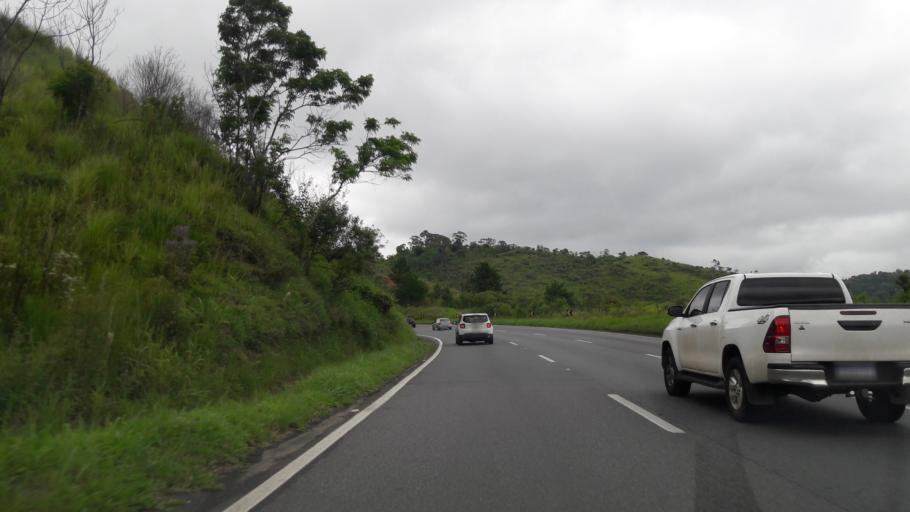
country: BR
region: Sao Paulo
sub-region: Cajati
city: Cajati
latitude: -24.9705
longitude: -48.4987
